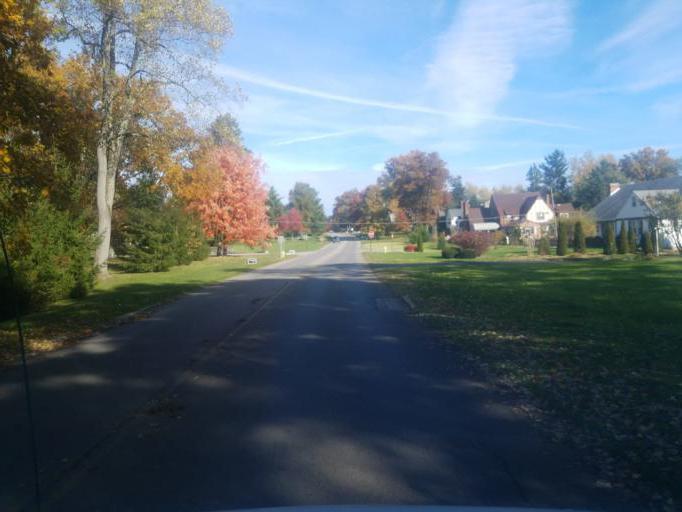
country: US
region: Ohio
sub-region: Richland County
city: Mansfield
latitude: 40.7404
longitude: -82.5409
